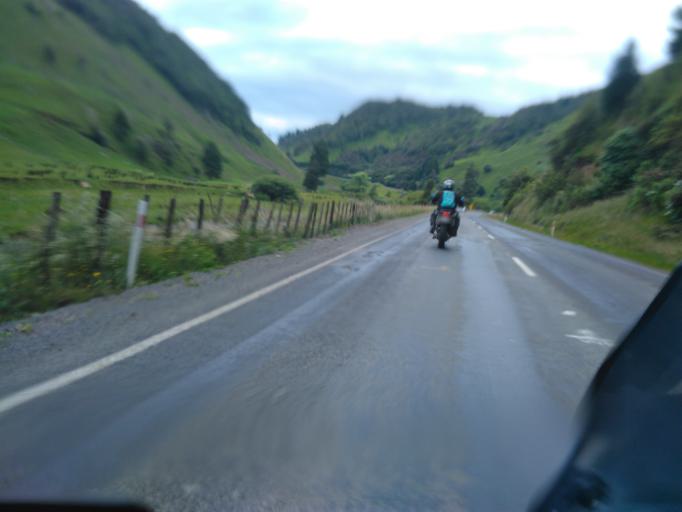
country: NZ
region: Bay of Plenty
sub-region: Opotiki District
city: Opotiki
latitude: -38.3768
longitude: 177.4827
